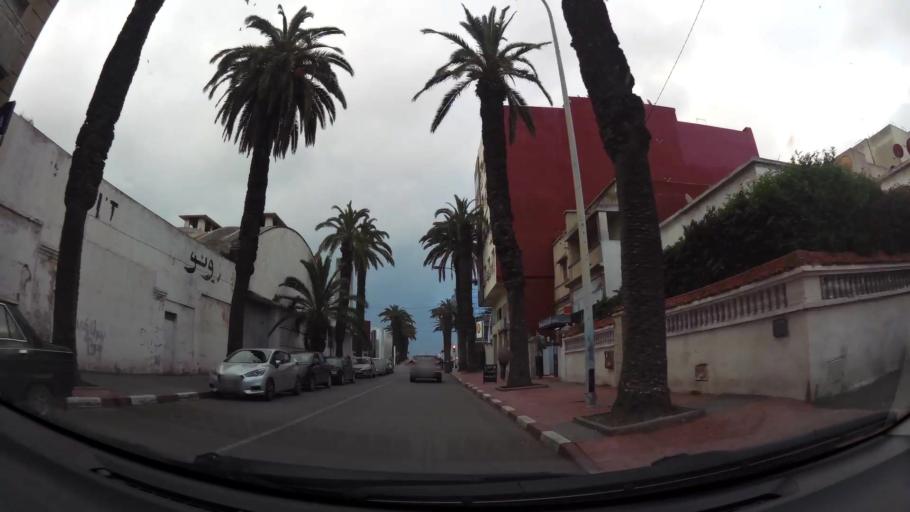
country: MA
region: Doukkala-Abda
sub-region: El-Jadida
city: El Jadida
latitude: 33.2489
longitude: -8.4997
